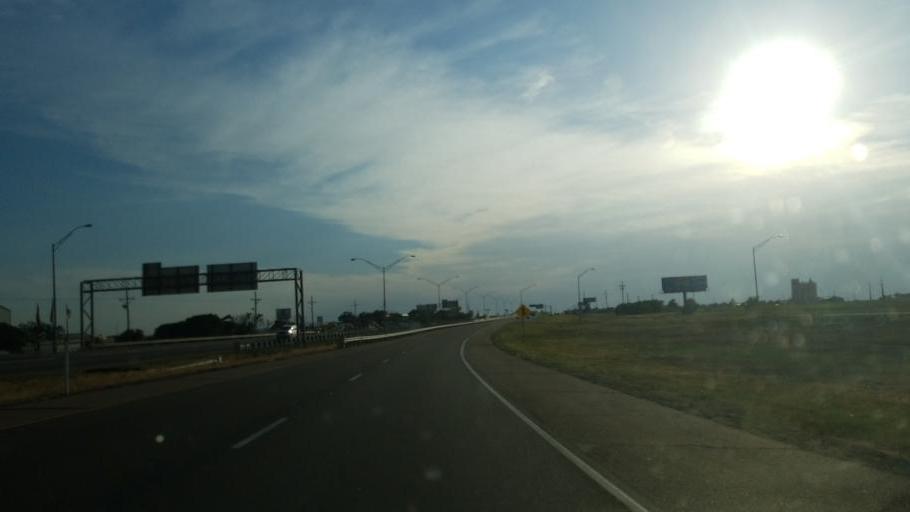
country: US
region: Texas
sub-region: Potter County
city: Amarillo
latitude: 35.1927
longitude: -101.6958
